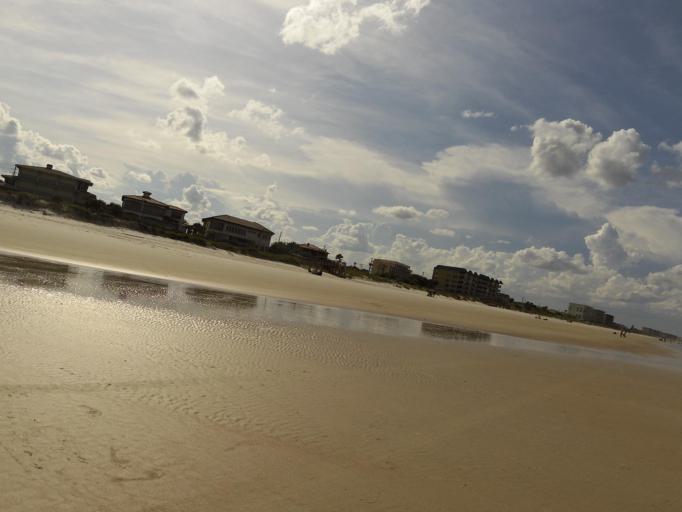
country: US
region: Florida
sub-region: Volusia County
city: Ponce Inlet
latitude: 29.0886
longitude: -80.9271
